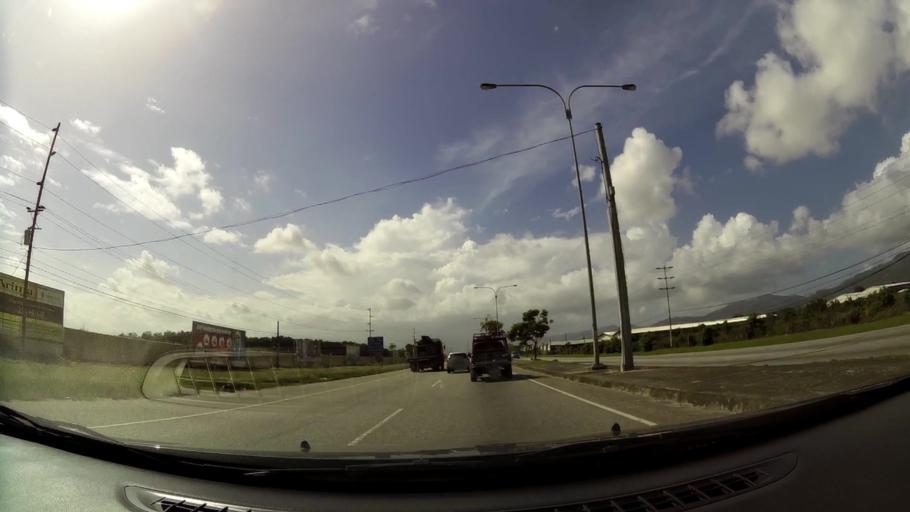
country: TT
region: Borough of Arima
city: Arima
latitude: 10.6105
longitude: -61.2933
